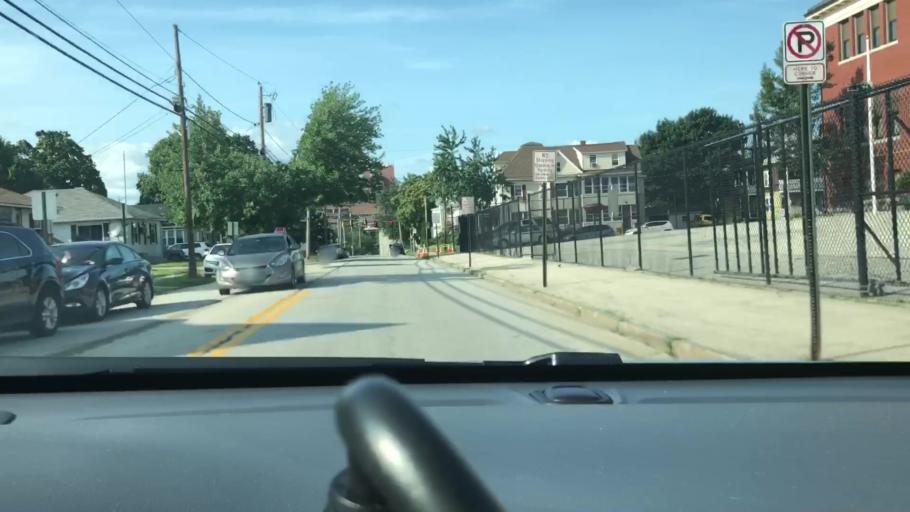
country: US
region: New Hampshire
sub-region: Hillsborough County
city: Manchester
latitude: 42.9800
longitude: -71.4381
